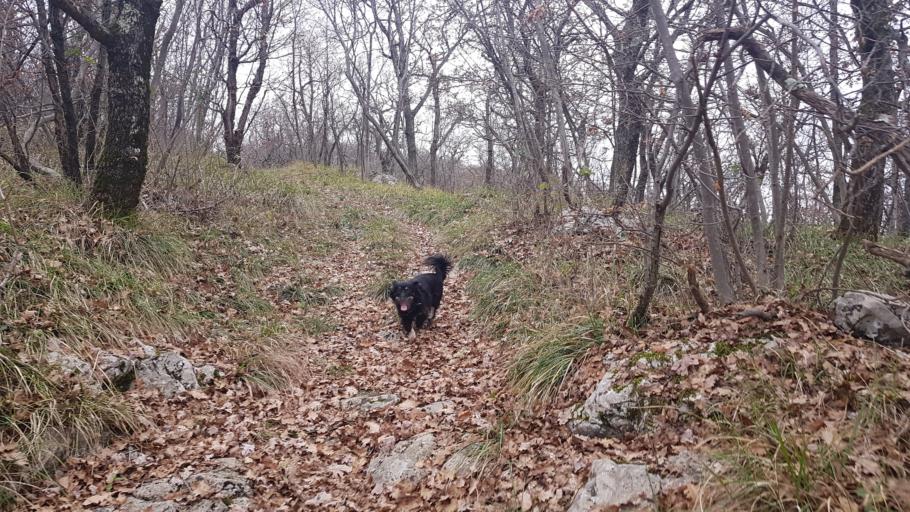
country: IT
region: Friuli Venezia Giulia
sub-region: Provincia di Trieste
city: Zolla
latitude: 45.7401
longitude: 13.7942
